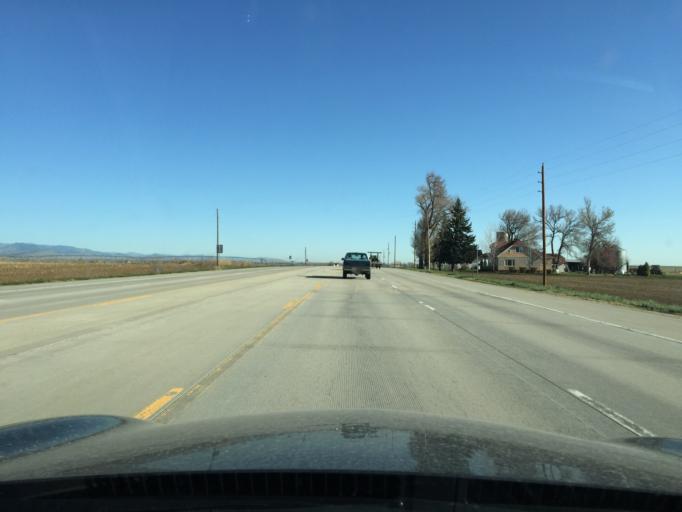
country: US
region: Colorado
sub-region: Boulder County
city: Niwot
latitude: 40.0958
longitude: -105.1029
